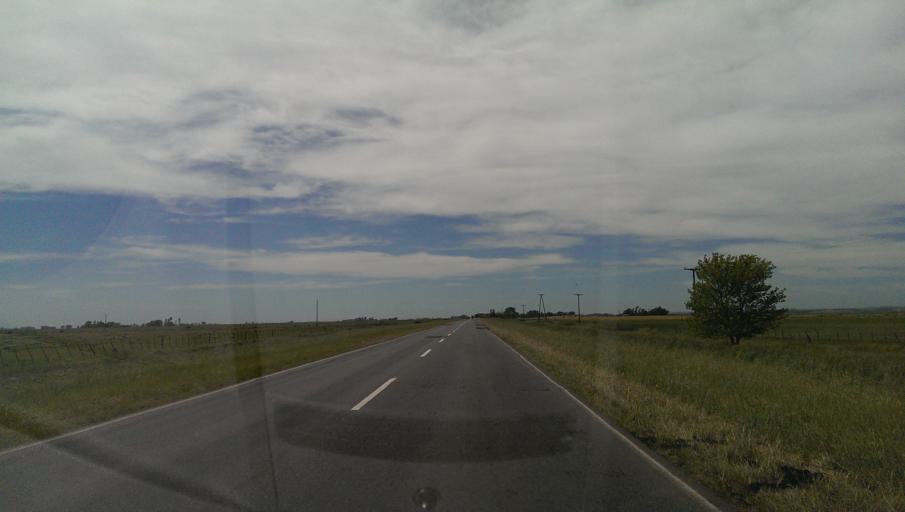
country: AR
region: Buenos Aires
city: Olavarria
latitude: -37.0445
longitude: -60.4403
